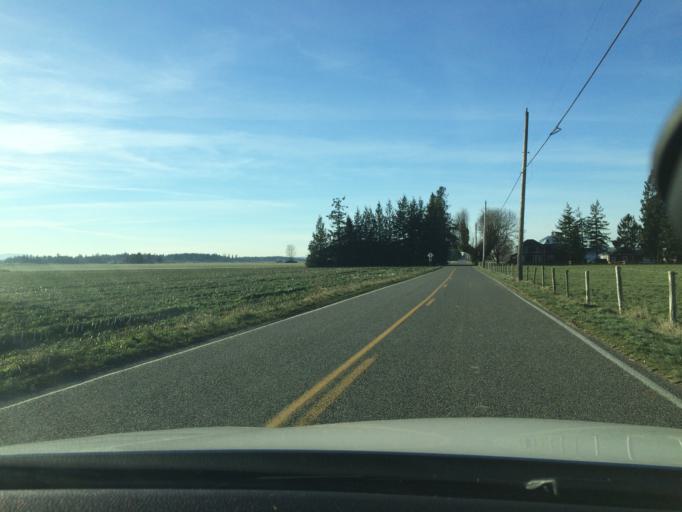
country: US
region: Washington
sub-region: Whatcom County
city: Lynden
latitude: 48.9277
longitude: -122.4049
